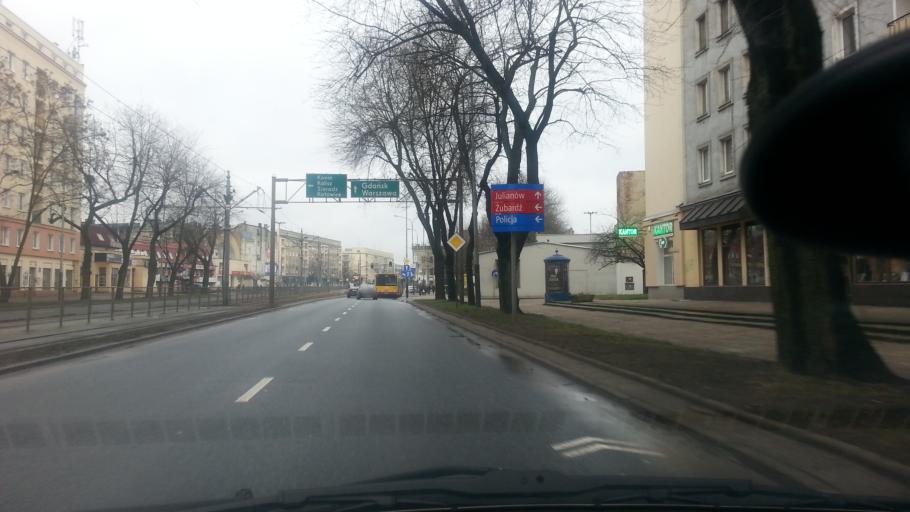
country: PL
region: Lodz Voivodeship
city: Lodz
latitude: 51.7853
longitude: 19.4498
